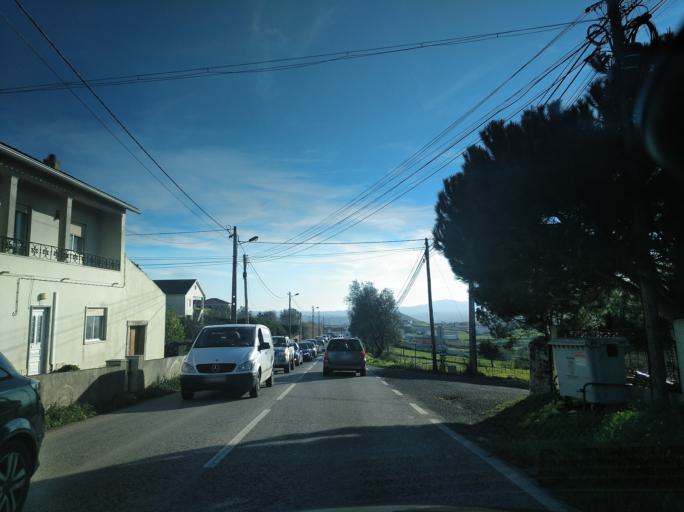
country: PT
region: Lisbon
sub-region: Mafra
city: Mafra
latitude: 38.9211
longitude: -9.3220
